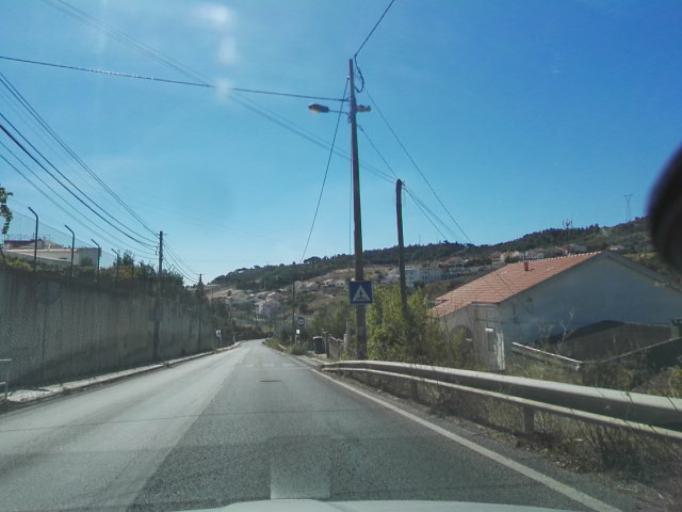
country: PT
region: Lisbon
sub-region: Vila Franca de Xira
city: Sao Joao dos Montes
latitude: 38.9361
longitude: -9.0239
